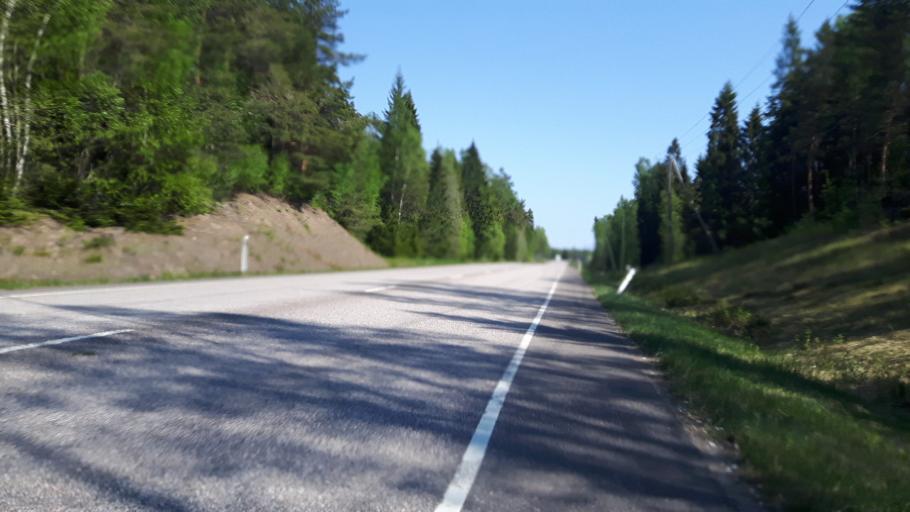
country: FI
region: Kymenlaakso
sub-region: Kotka-Hamina
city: Broby
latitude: 60.4892
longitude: 26.6517
